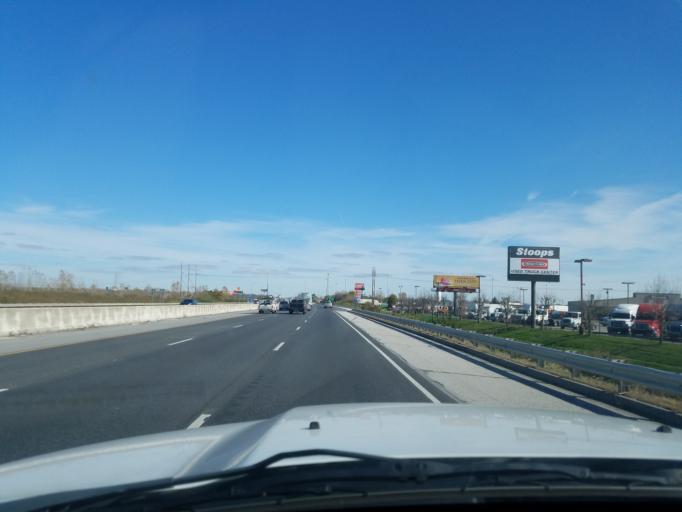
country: US
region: Indiana
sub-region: Marion County
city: Southport
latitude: 39.6936
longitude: -86.1962
